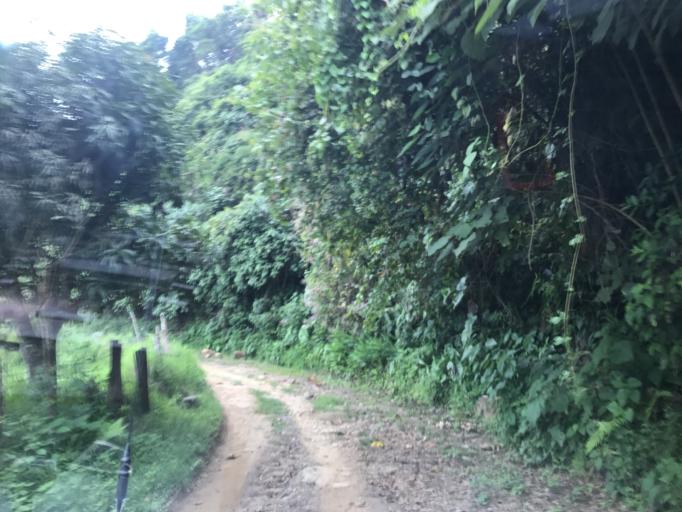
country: CO
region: Valle del Cauca
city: Obando
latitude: 4.5642
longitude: -75.8940
